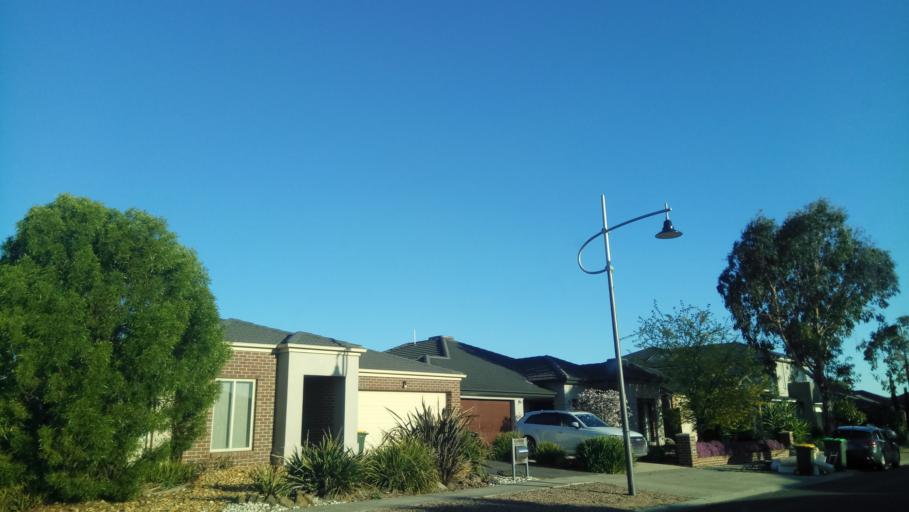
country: AU
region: Victoria
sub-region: Wyndham
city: Point Cook
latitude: -37.9117
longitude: 144.7422
